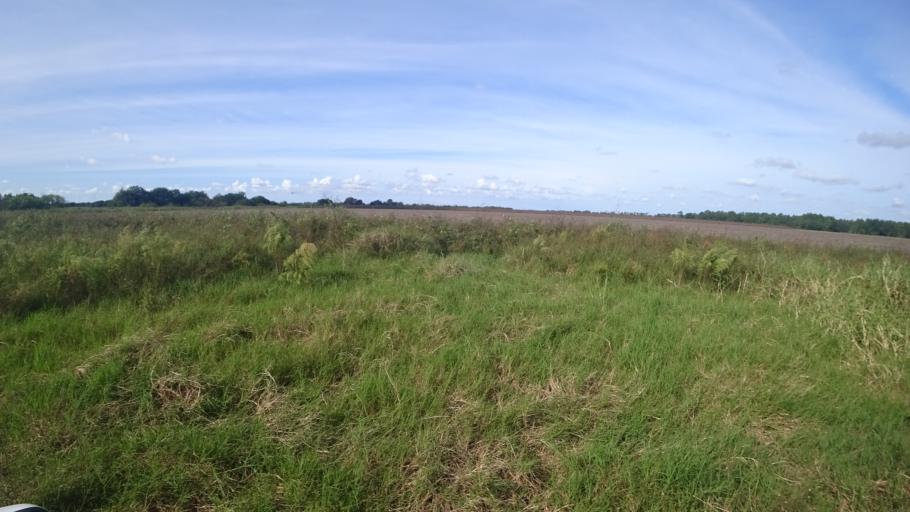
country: US
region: Florida
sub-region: Sarasota County
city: The Meadows
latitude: 27.4496
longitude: -82.3200
